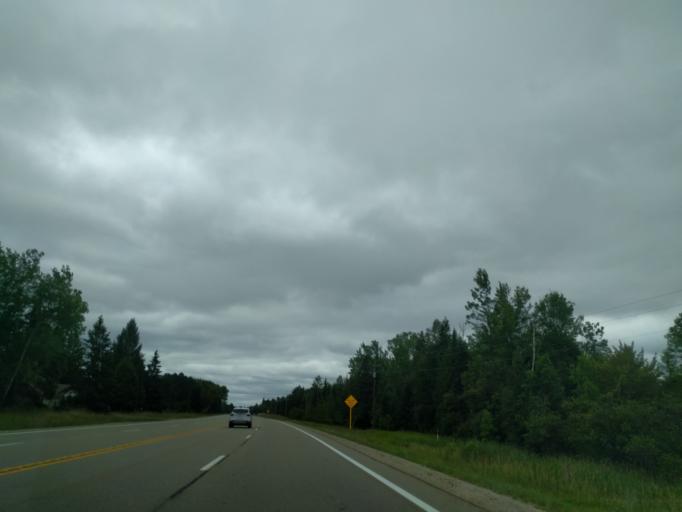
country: US
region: Michigan
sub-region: Delta County
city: Escanaba
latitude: 45.5312
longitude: -87.2862
